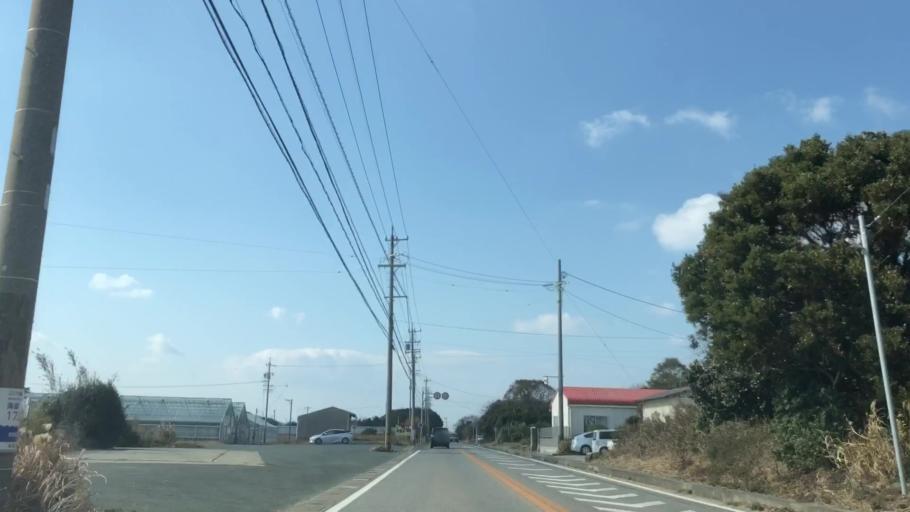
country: JP
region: Aichi
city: Tahara
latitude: 34.5904
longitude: 137.1059
